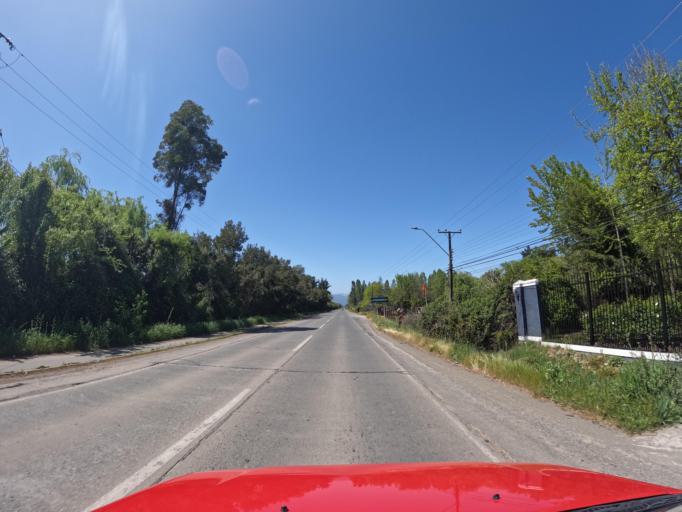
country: CL
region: Maule
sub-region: Provincia de Linares
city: Linares
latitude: -35.8342
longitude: -71.5431
